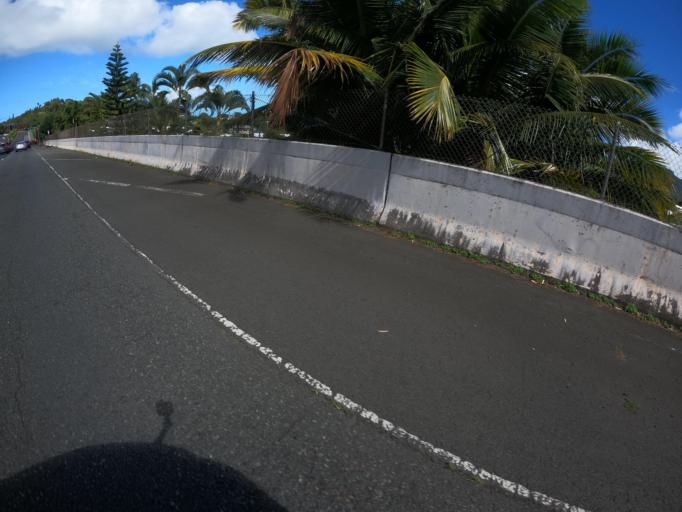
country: US
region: Hawaii
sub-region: Honolulu County
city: Kane'ohe
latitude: 21.4052
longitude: -157.8069
